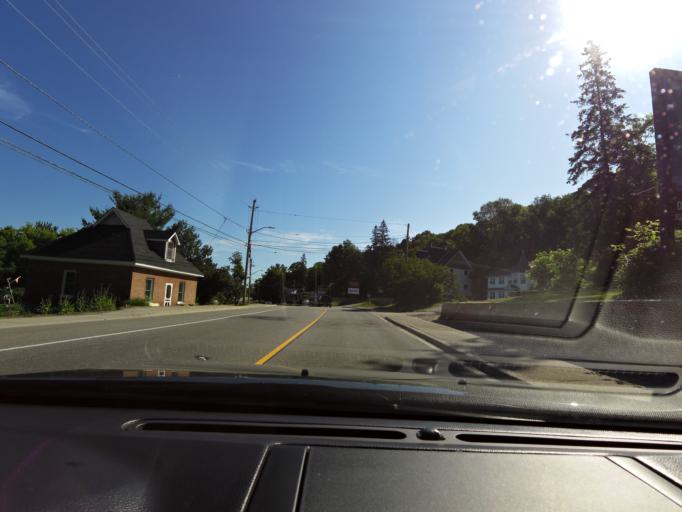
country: CA
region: Ontario
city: Huntsville
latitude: 45.3219
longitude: -79.2276
